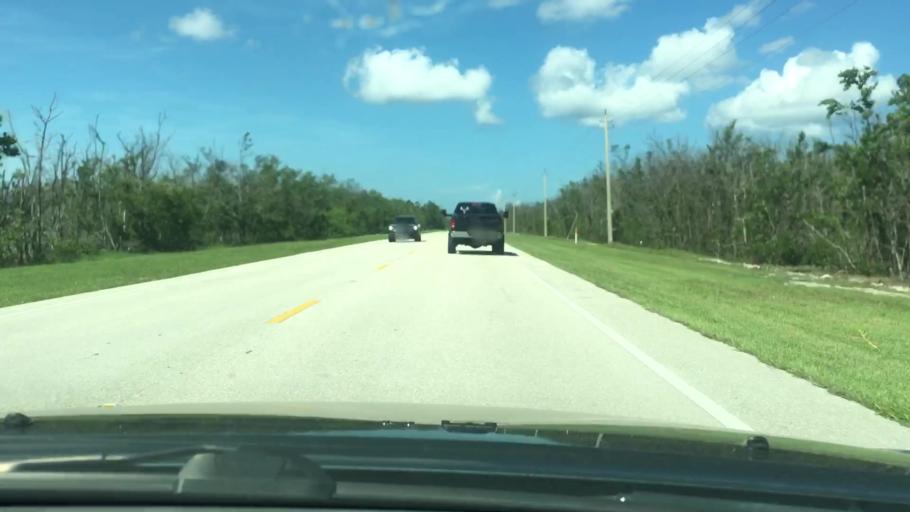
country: US
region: Florida
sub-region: Collier County
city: Marco
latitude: 25.9322
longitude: -81.6616
